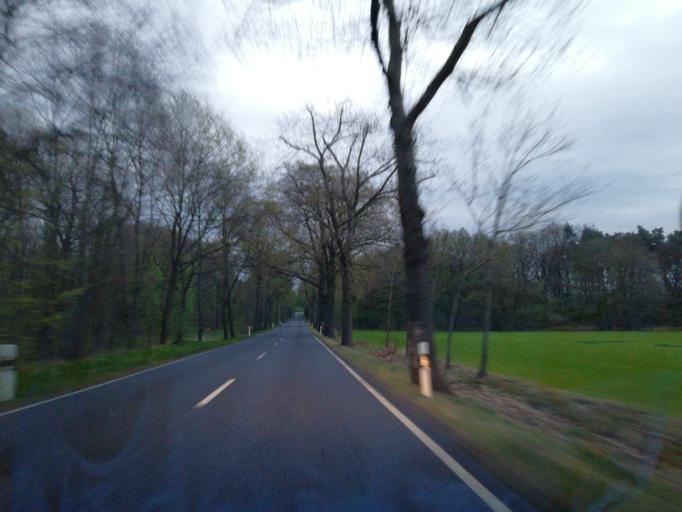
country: DE
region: Brandenburg
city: Calau
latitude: 51.7549
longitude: 13.9282
